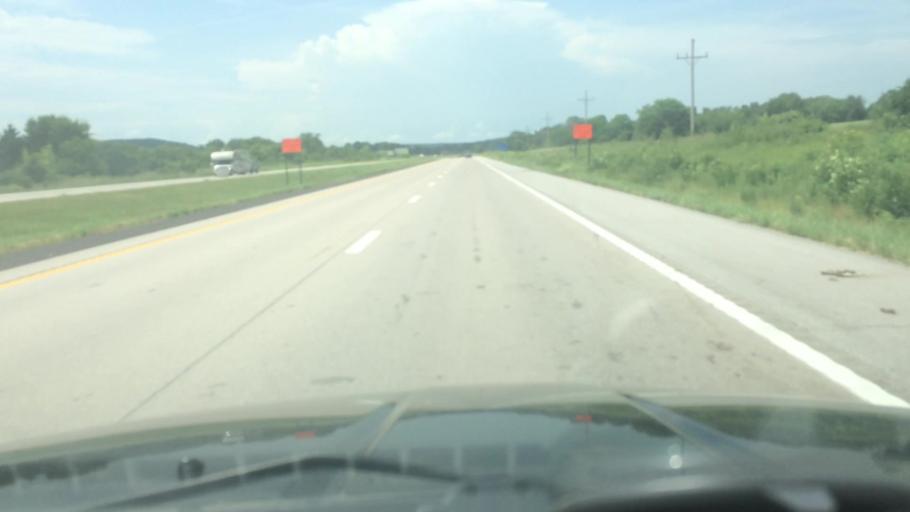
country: US
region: Missouri
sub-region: Polk County
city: Humansville
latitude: 37.8107
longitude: -93.6047
